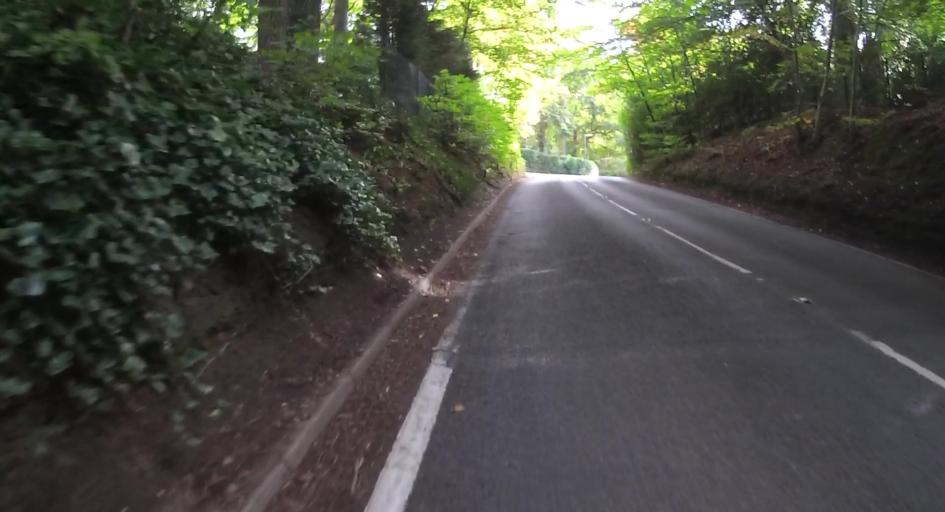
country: GB
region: England
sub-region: Surrey
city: Seale
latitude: 51.2082
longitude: -0.7493
